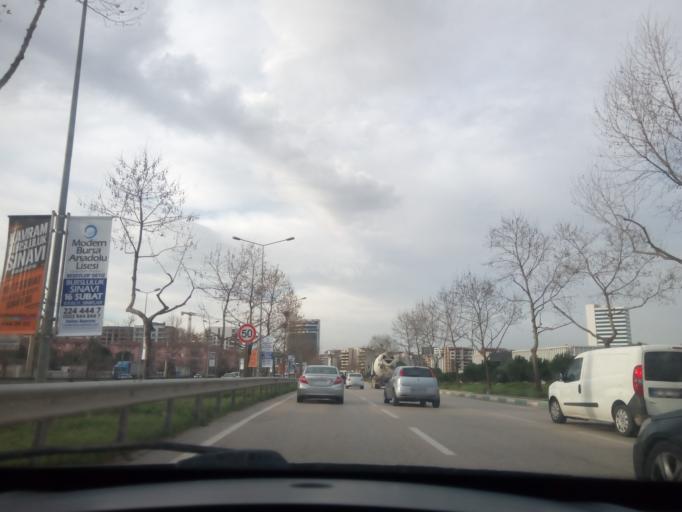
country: TR
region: Bursa
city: Niluefer
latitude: 40.2231
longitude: 28.9564
